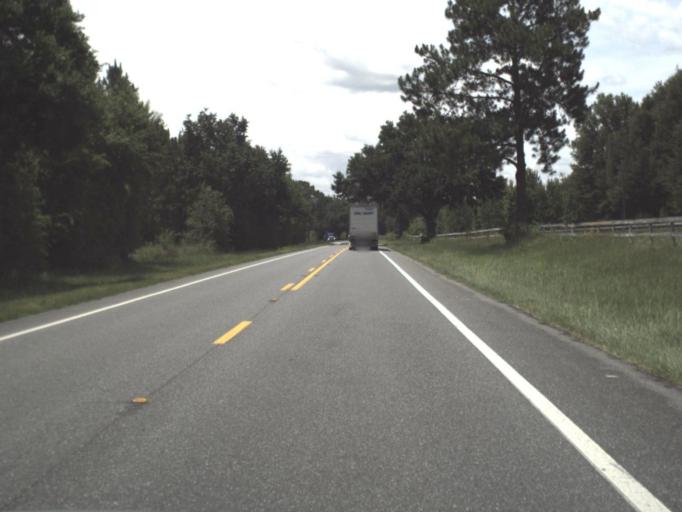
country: US
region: Florida
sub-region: Alachua County
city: Archer
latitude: 29.5830
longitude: -82.5535
